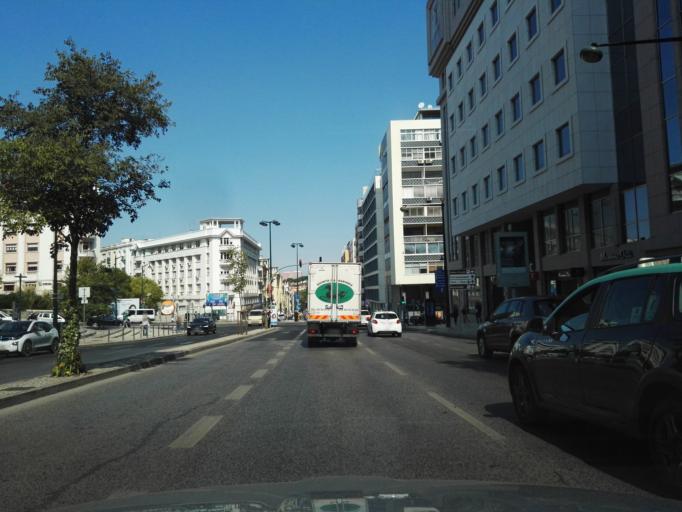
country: PT
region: Lisbon
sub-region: Lisbon
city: Lisbon
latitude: 38.7337
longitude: -9.1534
